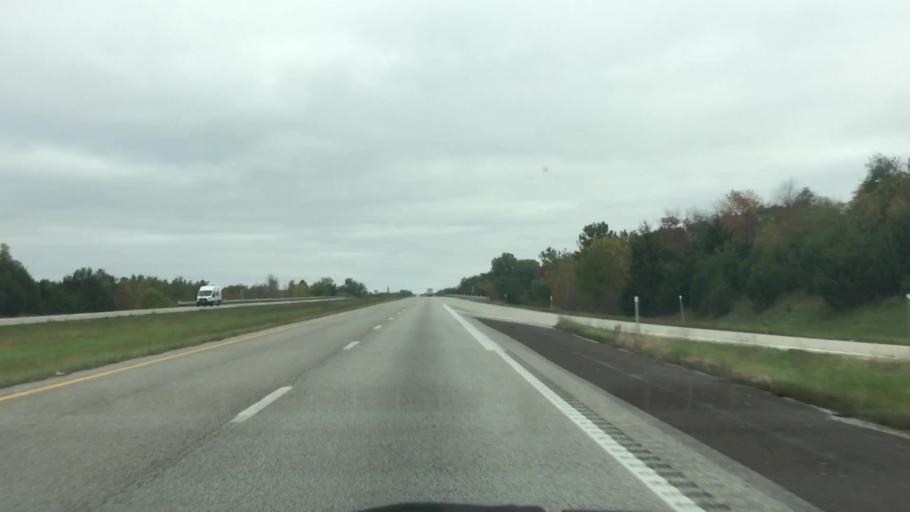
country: US
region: Missouri
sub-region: Clinton County
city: Cameron
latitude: 39.9015
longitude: -94.1502
